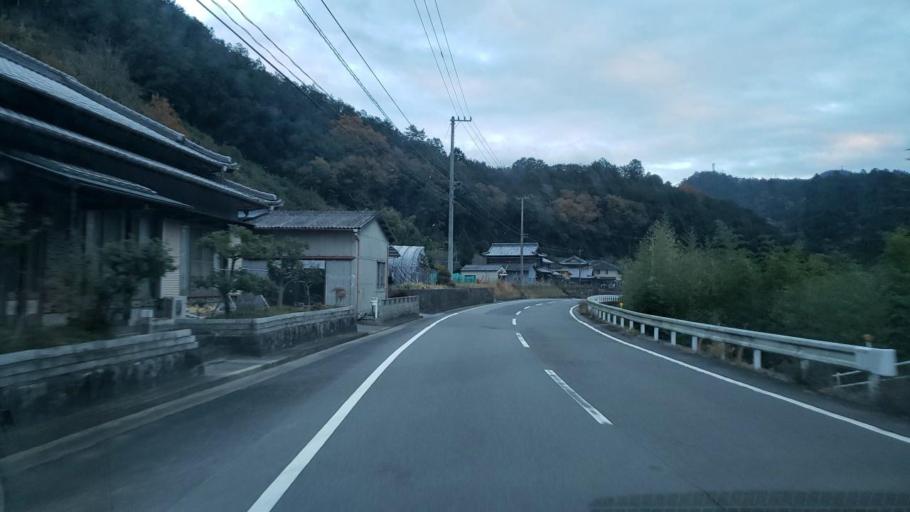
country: JP
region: Tokushima
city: Kamojimacho-jogejima
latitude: 34.1982
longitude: 134.2809
